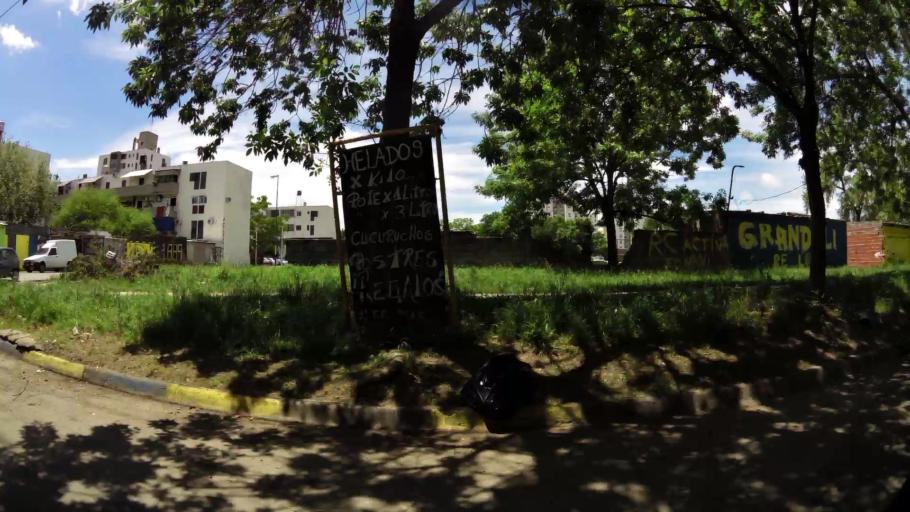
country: AR
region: Santa Fe
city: Gobernador Galvez
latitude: -32.9925
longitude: -60.6248
